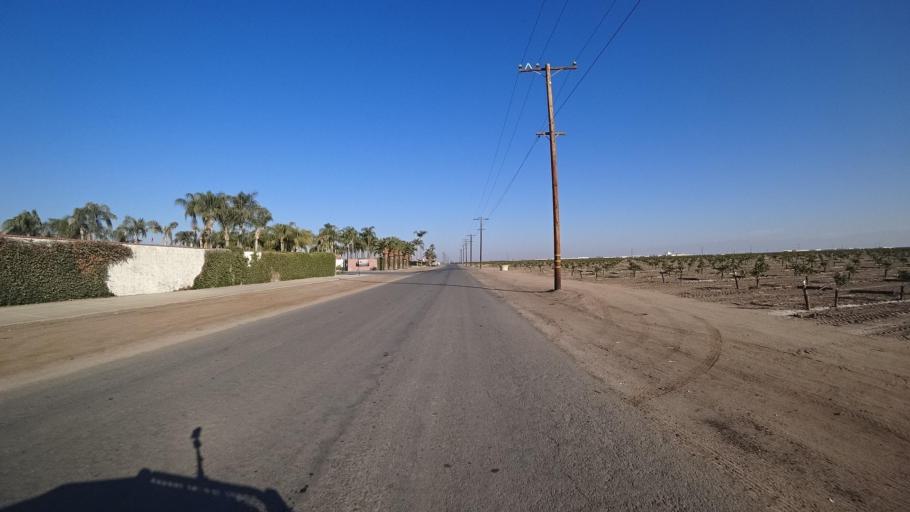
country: US
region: California
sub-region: Tulare County
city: Richgrove
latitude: 35.7870
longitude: -119.1608
